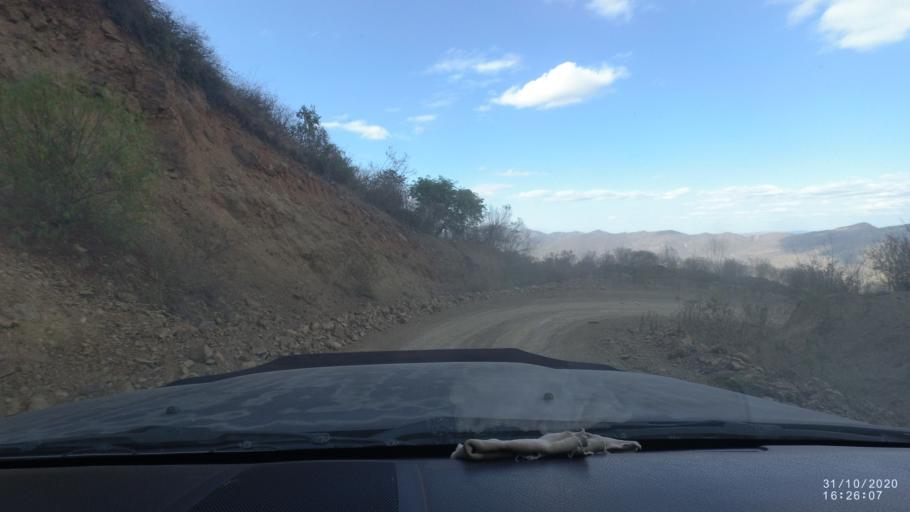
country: BO
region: Chuquisaca
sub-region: Provincia Zudanez
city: Mojocoya
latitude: -18.3963
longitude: -64.5868
